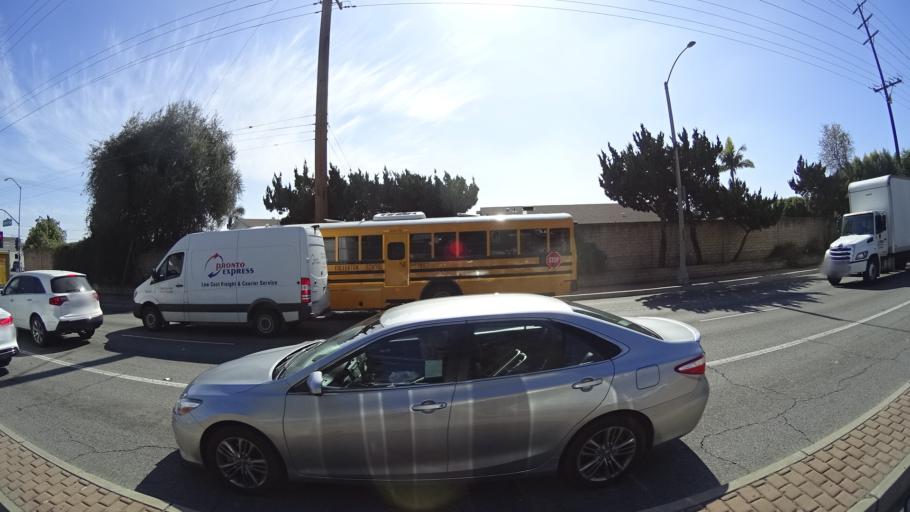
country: US
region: California
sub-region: Orange County
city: Brea
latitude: 33.9174
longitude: -117.9160
